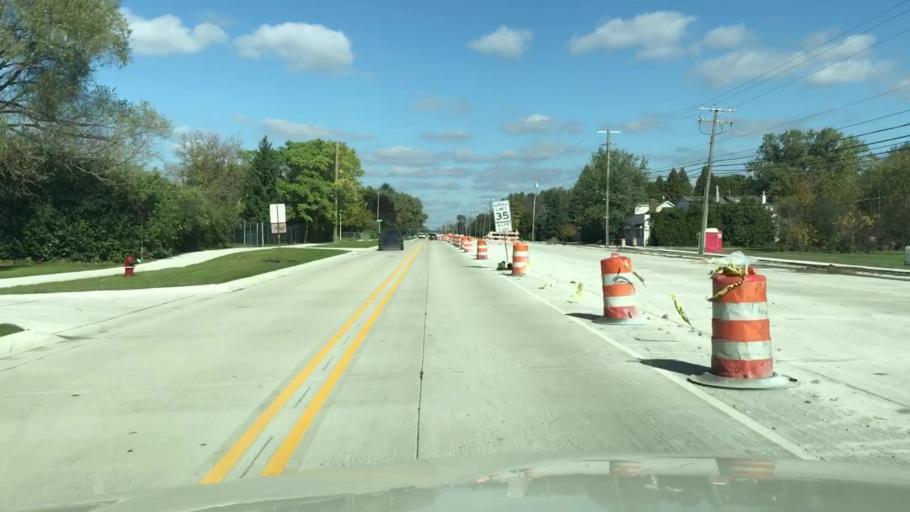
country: US
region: Michigan
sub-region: Oakland County
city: Troy
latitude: 42.6003
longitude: -83.0904
